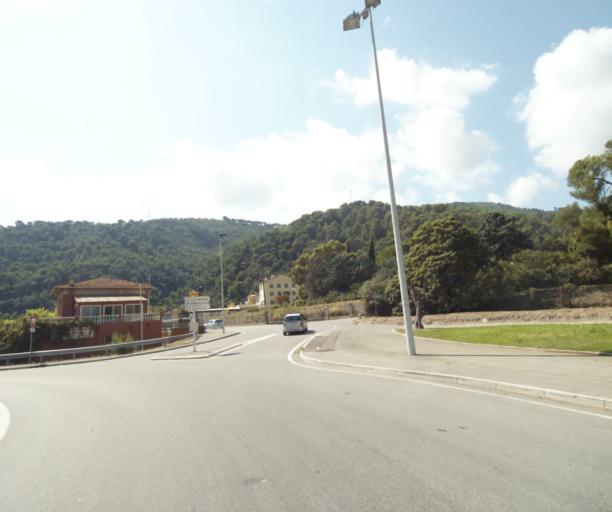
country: FR
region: Provence-Alpes-Cote d'Azur
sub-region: Departement des Alpes-Maritimes
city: Cantaron
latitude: 43.7620
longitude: 7.3196
